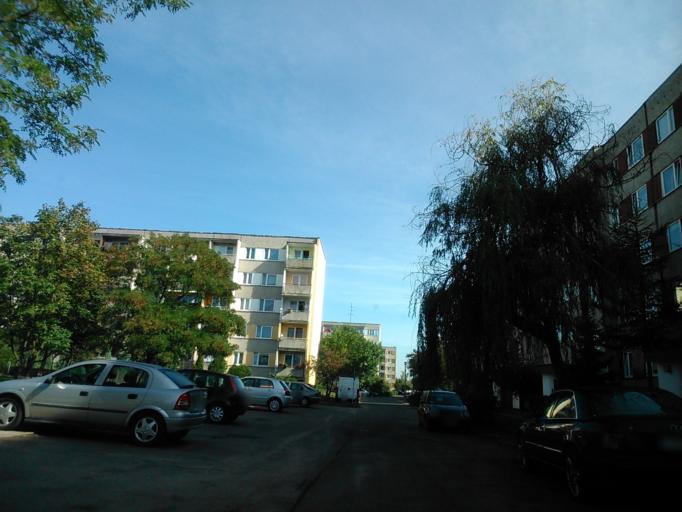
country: PL
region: Kujawsko-Pomorskie
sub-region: Powiat golubsko-dobrzynski
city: Golub-Dobrzyn
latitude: 53.1010
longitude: 19.0566
